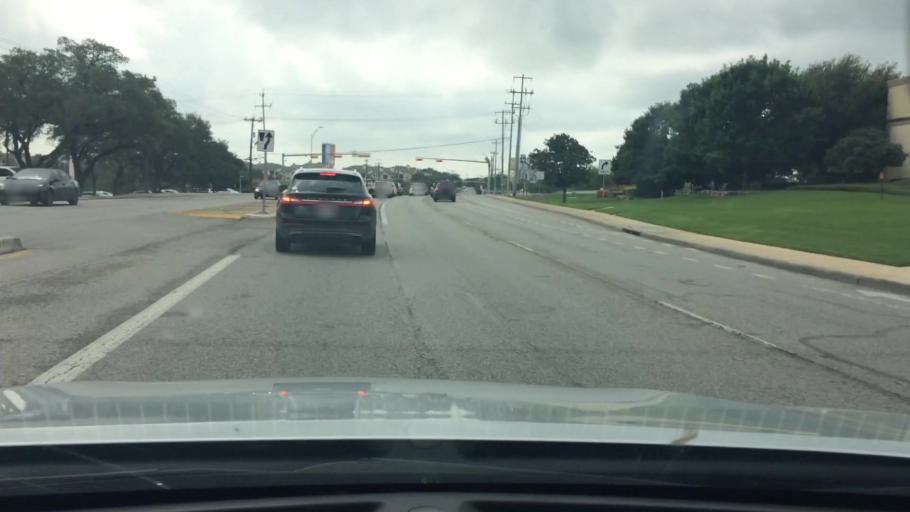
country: US
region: Texas
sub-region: Bexar County
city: Hollywood Park
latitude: 29.6104
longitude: -98.5085
